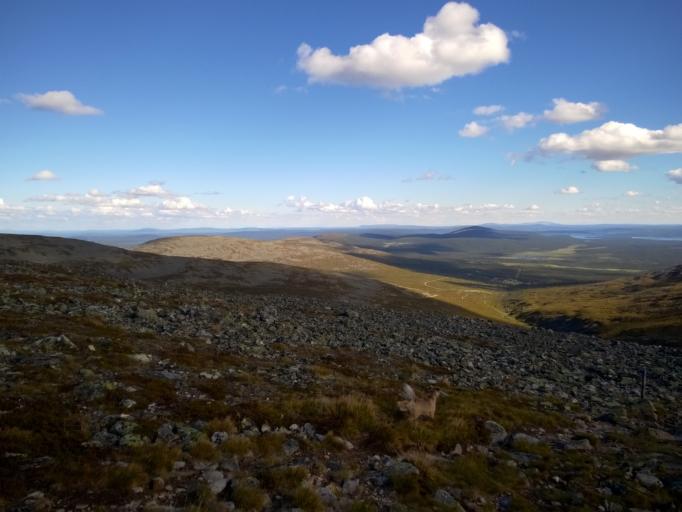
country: FI
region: Lapland
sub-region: Tunturi-Lappi
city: Muonio
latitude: 68.0729
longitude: 24.0490
